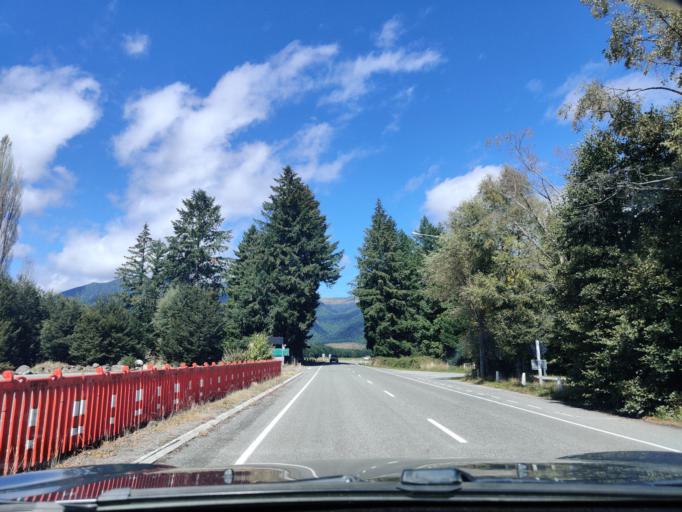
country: NZ
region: West Coast
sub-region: Buller District
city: Westport
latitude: -42.3355
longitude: 172.1828
